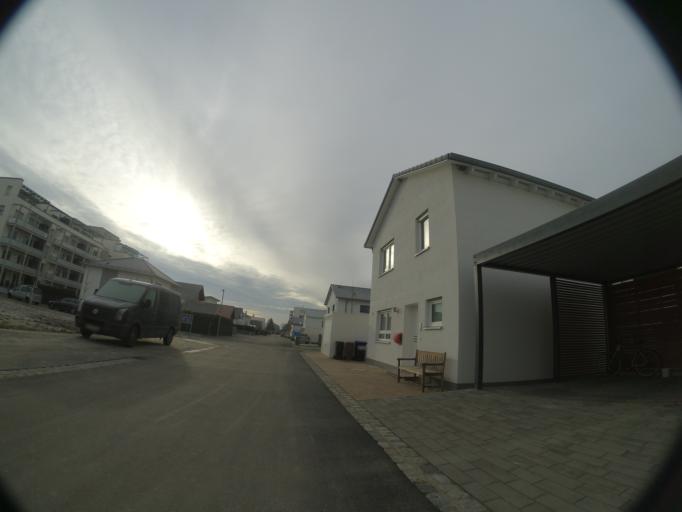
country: DE
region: Bavaria
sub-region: Swabia
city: Neu-Ulm
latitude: 48.4353
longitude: 10.0194
